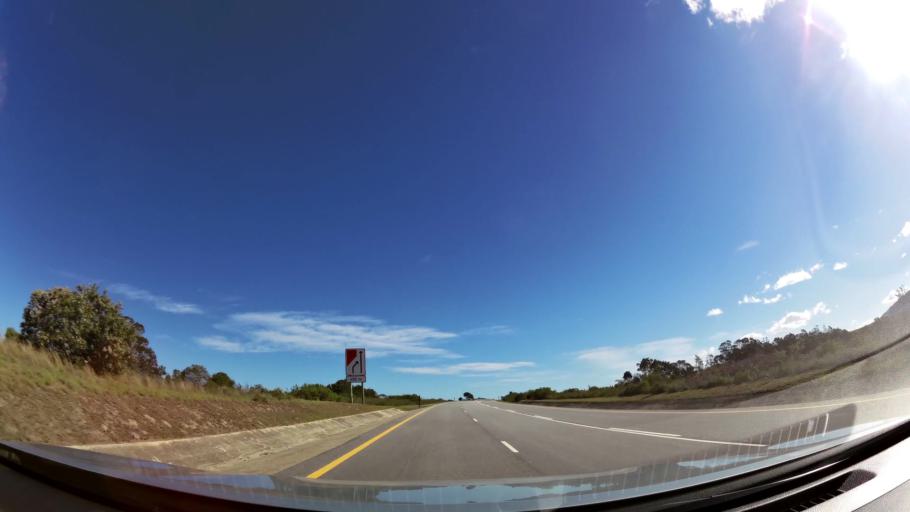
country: ZA
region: Eastern Cape
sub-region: Cacadu District Municipality
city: Kruisfontein
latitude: -34.0093
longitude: 24.6627
